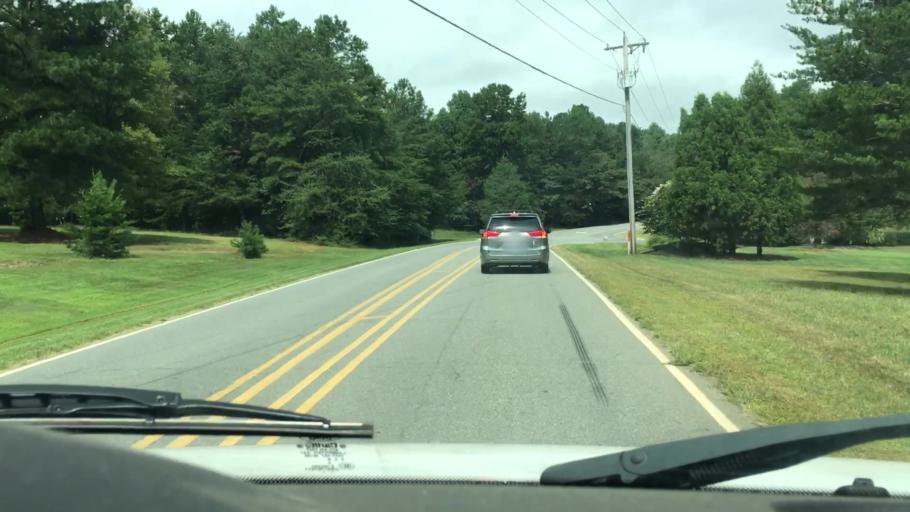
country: US
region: North Carolina
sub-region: Gaston County
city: Davidson
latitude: 35.5167
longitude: -80.7992
